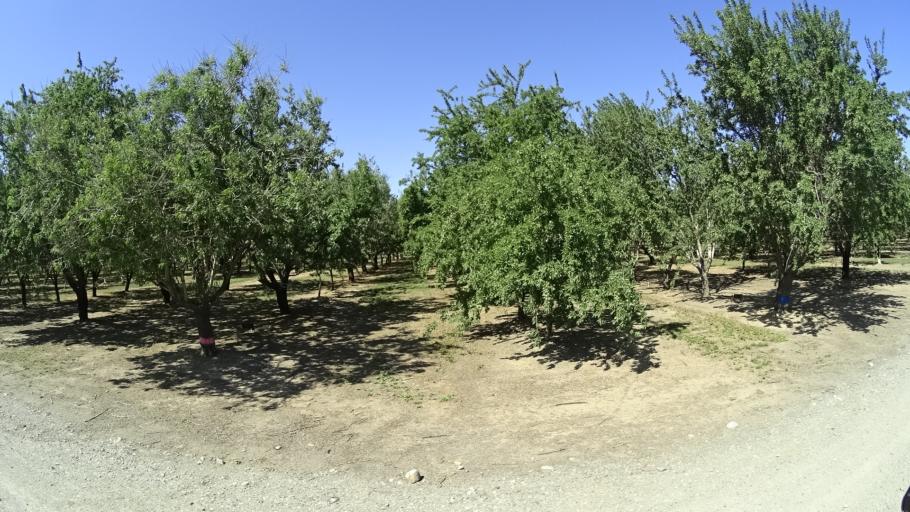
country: US
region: California
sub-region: Glenn County
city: Orland
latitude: 39.6838
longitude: -122.1592
